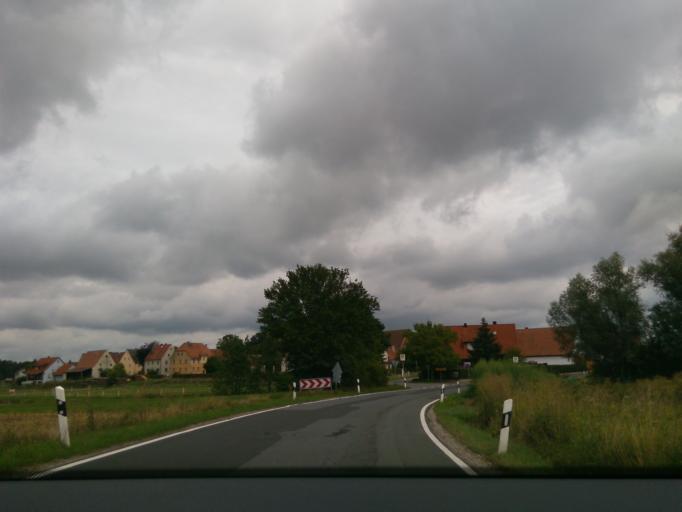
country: DE
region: Bavaria
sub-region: Regierungsbezirk Mittelfranken
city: Gremsdorf
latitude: 49.6666
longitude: 10.8047
